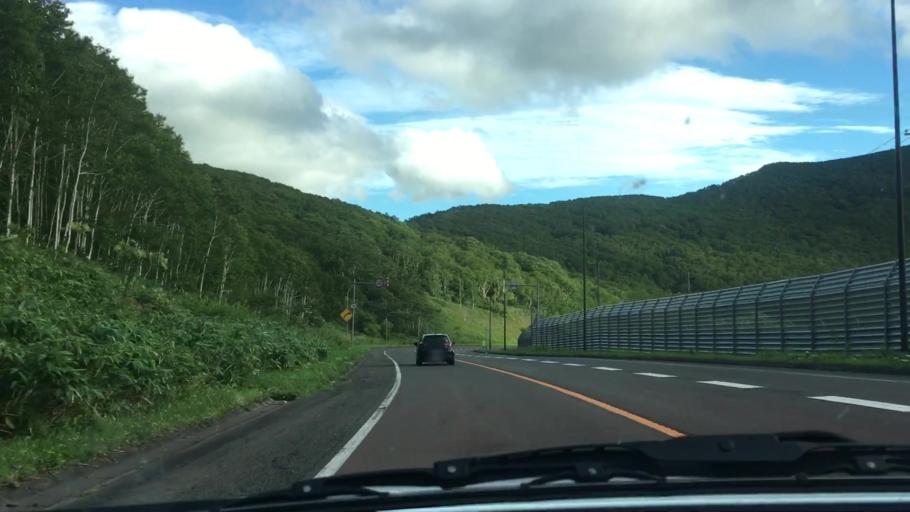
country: JP
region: Hokkaido
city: Shimo-furano
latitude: 43.1320
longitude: 142.7623
